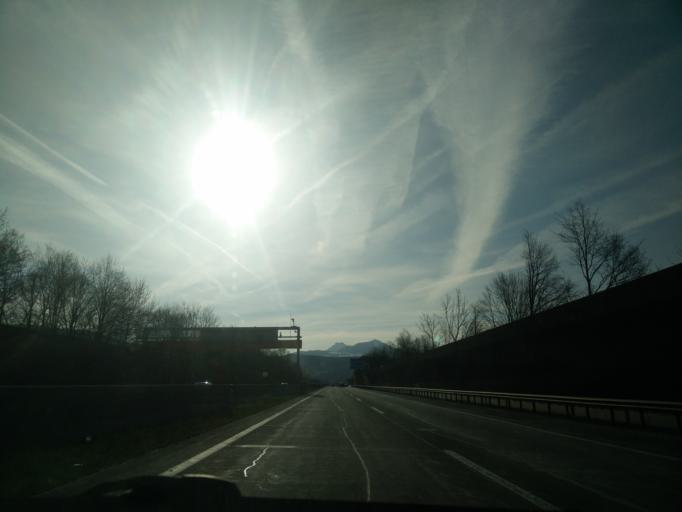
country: AT
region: Salzburg
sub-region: Politischer Bezirk Salzburg-Umgebung
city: Grodig
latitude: 47.7431
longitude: 13.0419
